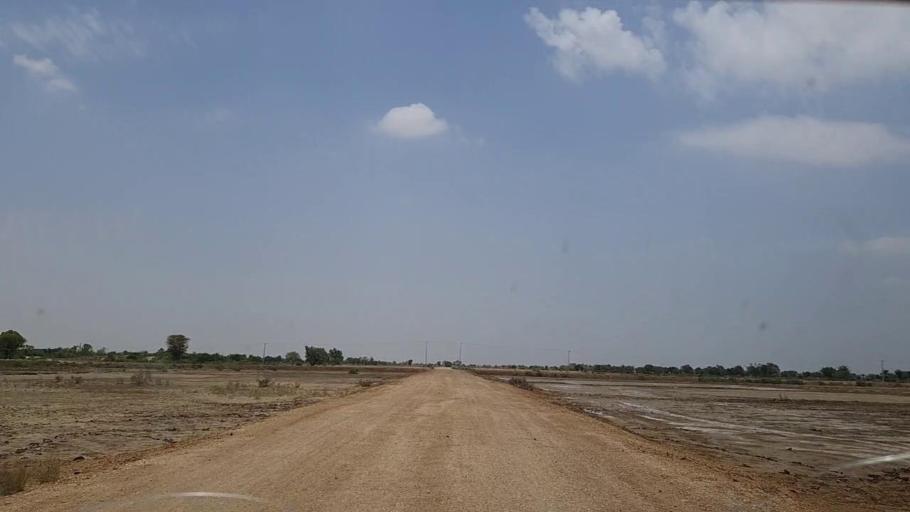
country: PK
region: Sindh
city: Phulji
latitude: 26.8154
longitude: 67.6340
